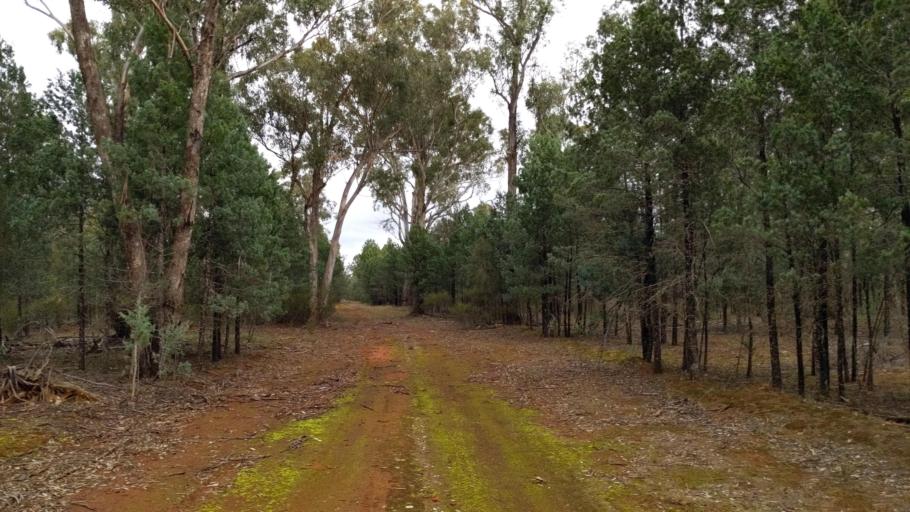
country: AU
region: New South Wales
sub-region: Coolamon
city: Coolamon
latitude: -34.8415
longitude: 146.9335
